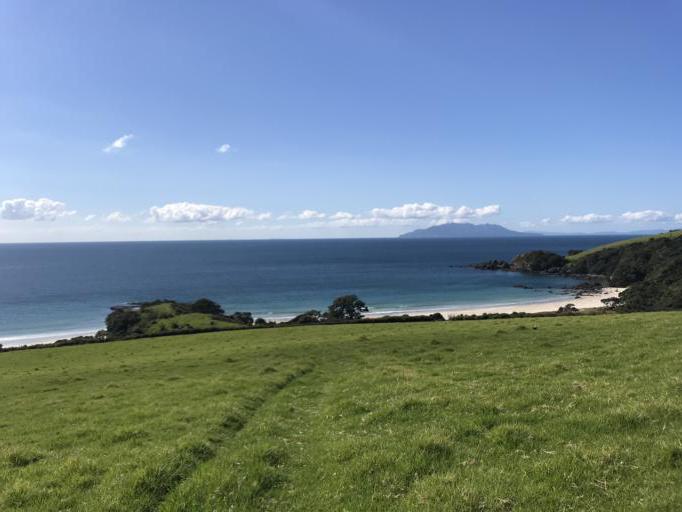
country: NZ
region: Auckland
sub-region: Auckland
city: Warkworth
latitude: -36.3720
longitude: 174.8352
